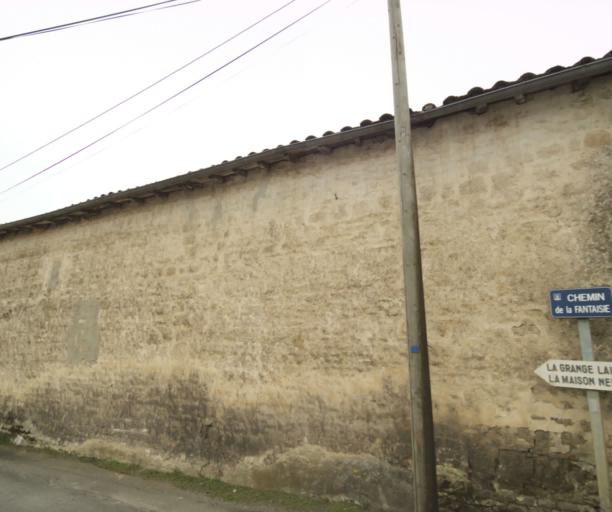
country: FR
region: Poitou-Charentes
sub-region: Departement des Deux-Sevres
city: Bessines
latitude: 46.3113
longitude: -0.4939
